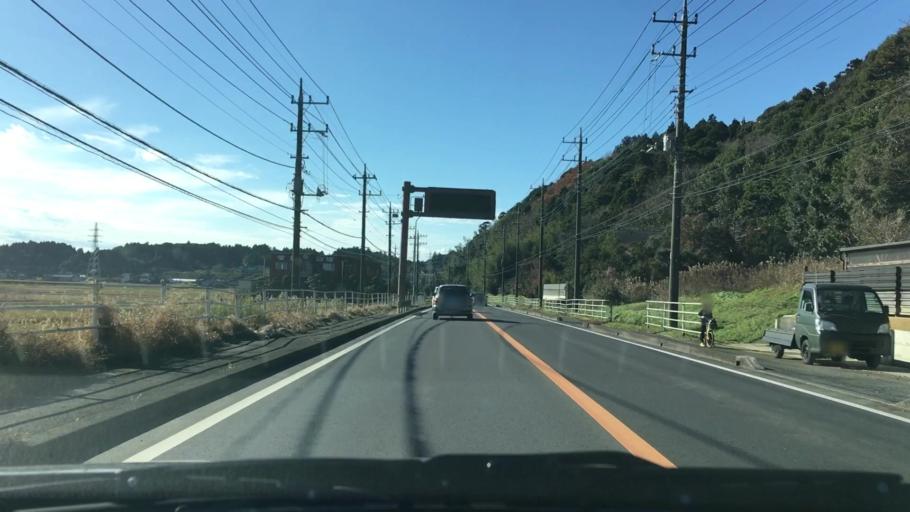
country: JP
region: Chiba
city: Omigawa
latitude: 35.8461
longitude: 140.5759
